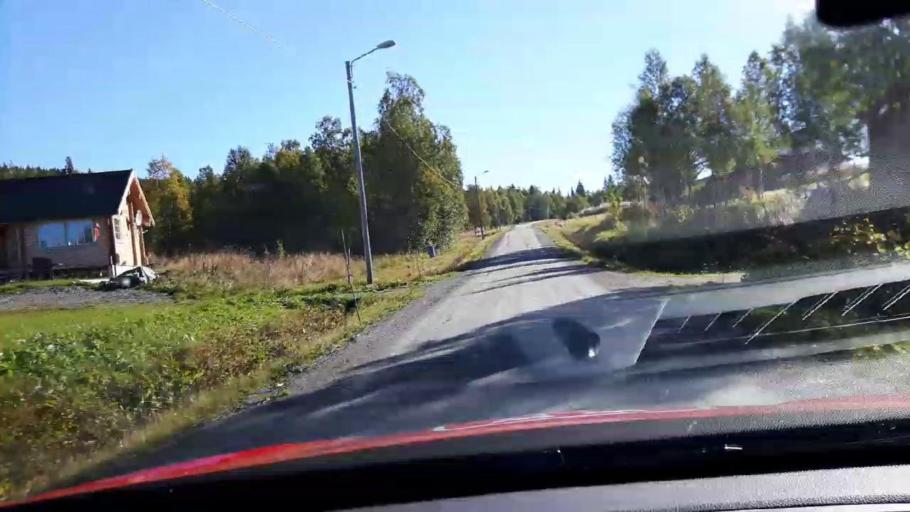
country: NO
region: Nord-Trondelag
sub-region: Lierne
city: Sandvika
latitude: 64.6447
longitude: 13.7750
